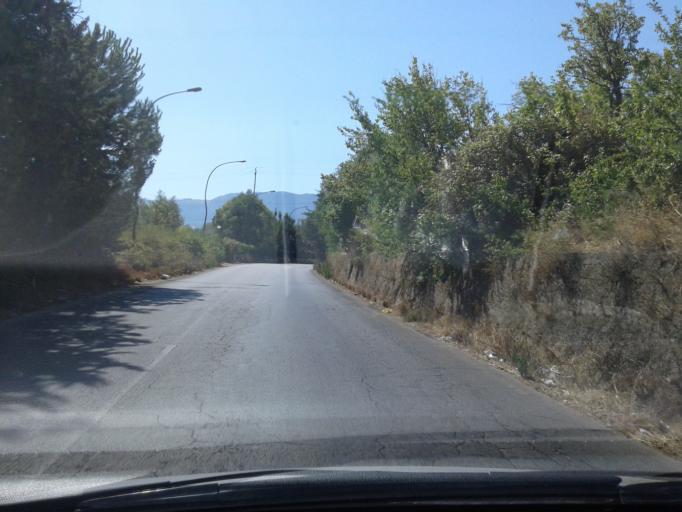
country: IT
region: Sicily
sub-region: Palermo
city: Cannizzaro-Favara
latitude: 38.0737
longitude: 13.2768
